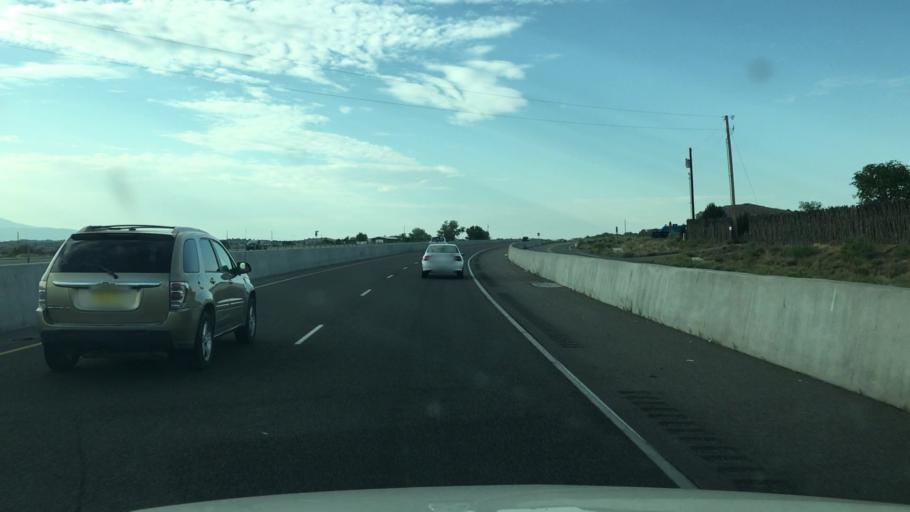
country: US
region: New Mexico
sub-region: Santa Fe County
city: El Valle de Arroyo Seco
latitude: 35.9541
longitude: -106.0215
